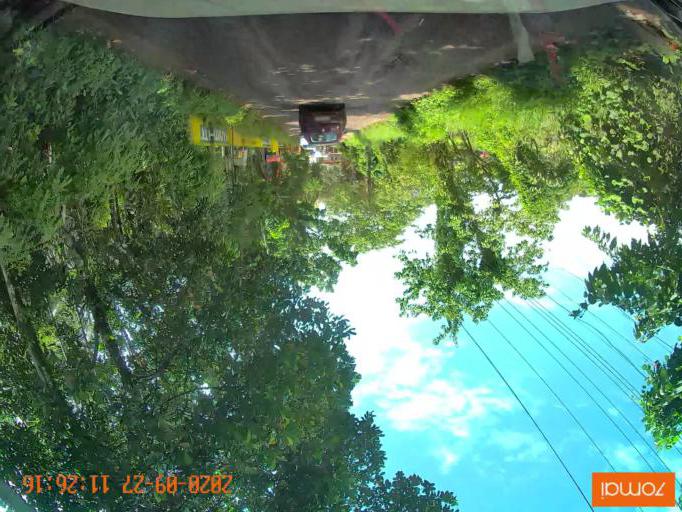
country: IN
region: Kerala
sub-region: Thrissur District
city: Thanniyam
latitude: 10.4151
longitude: 76.1541
